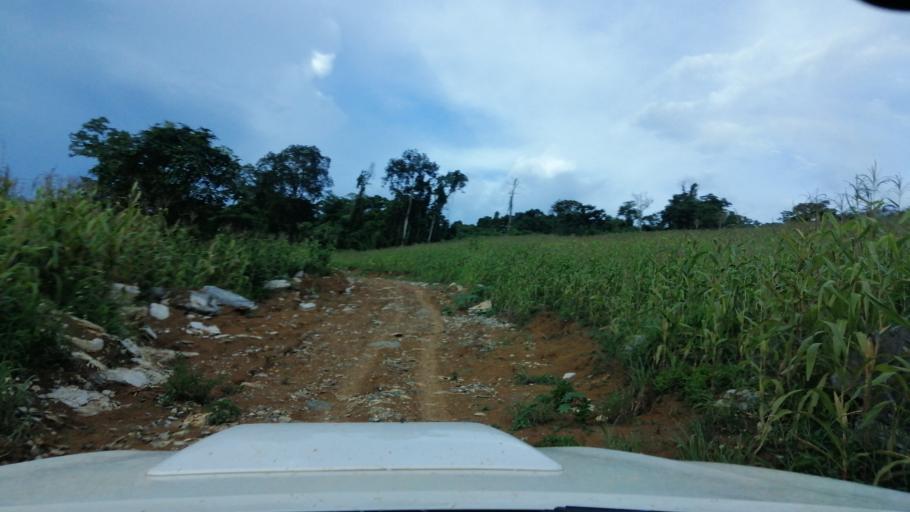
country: TH
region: Nan
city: Chaloem Phra Kiat
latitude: 19.7585
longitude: 101.1147
